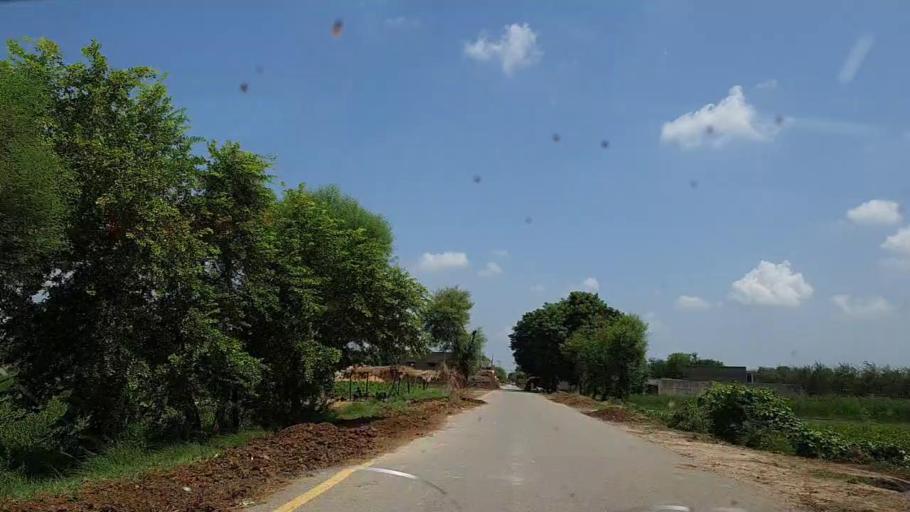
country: PK
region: Sindh
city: Tharu Shah
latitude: 26.9649
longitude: 68.0963
